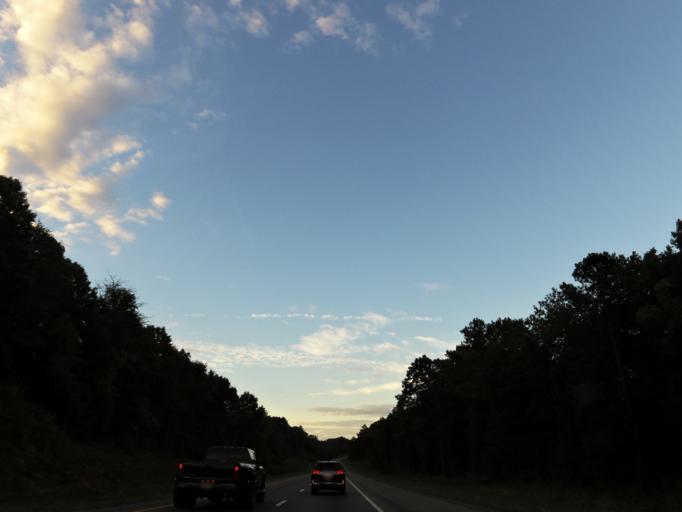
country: US
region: Tennessee
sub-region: Meigs County
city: Decatur
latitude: 35.3653
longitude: -84.7375
